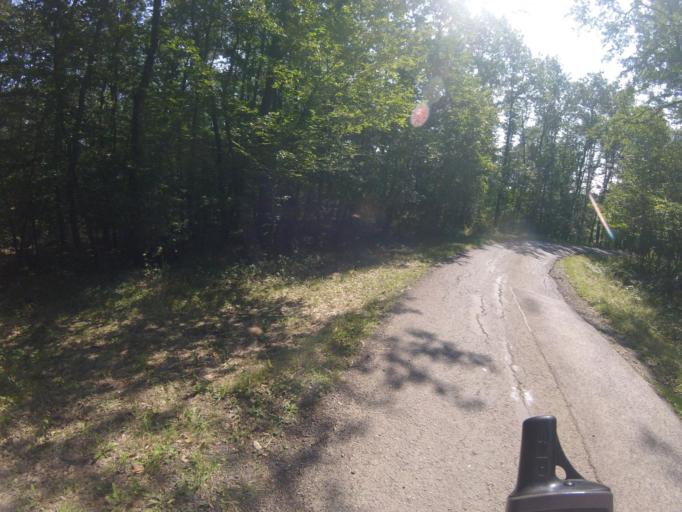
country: HU
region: Nograd
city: Bujak
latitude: 47.9023
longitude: 19.5153
